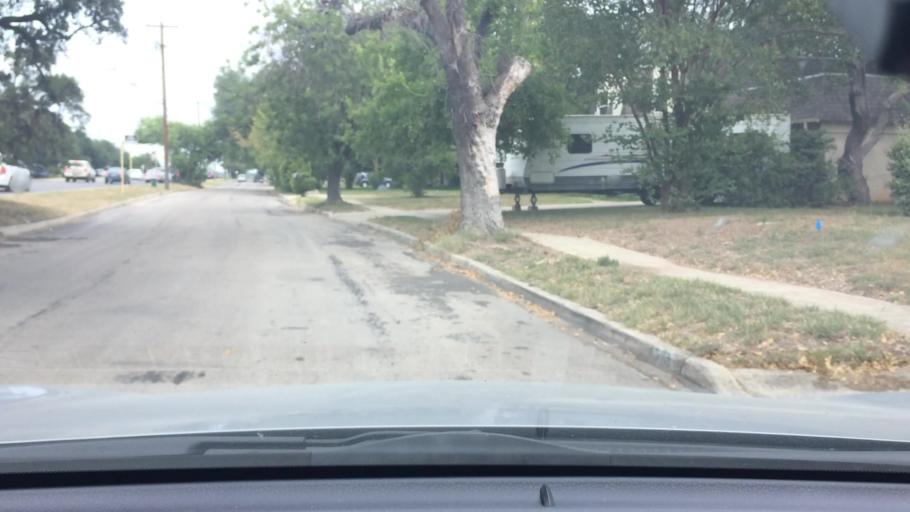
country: US
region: Texas
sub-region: Bexar County
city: Leon Valley
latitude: 29.4662
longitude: -98.6127
